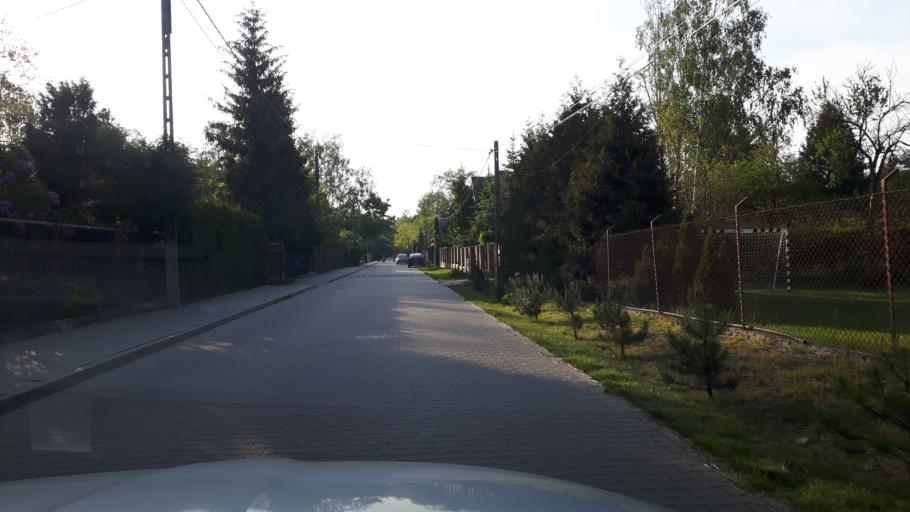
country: PL
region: Masovian Voivodeship
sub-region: Warszawa
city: Rembertow
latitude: 52.2744
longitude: 21.1583
